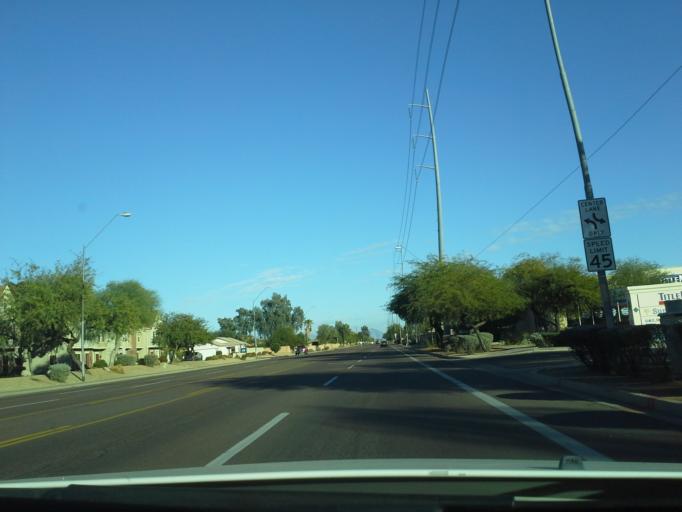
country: US
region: Arizona
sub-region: Maricopa County
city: Glendale
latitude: 33.6546
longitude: -112.1325
